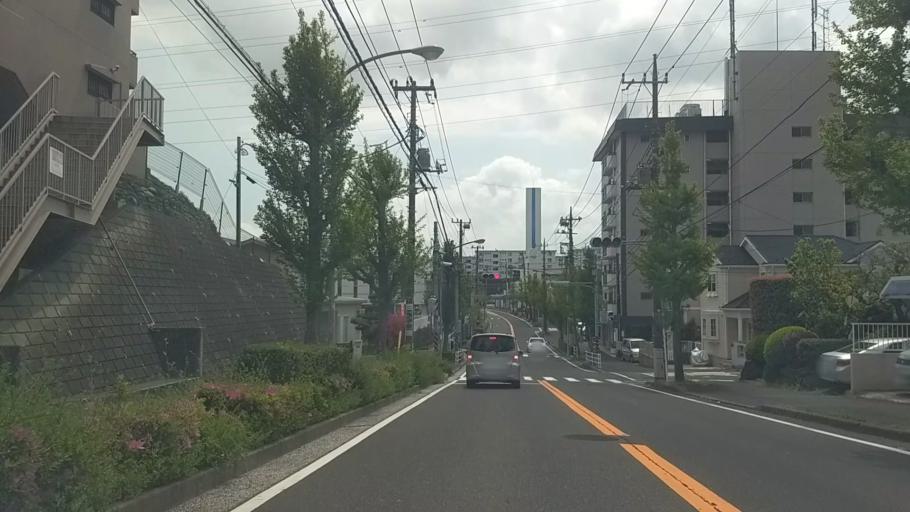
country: JP
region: Kanagawa
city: Kamakura
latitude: 35.3780
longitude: 139.5926
